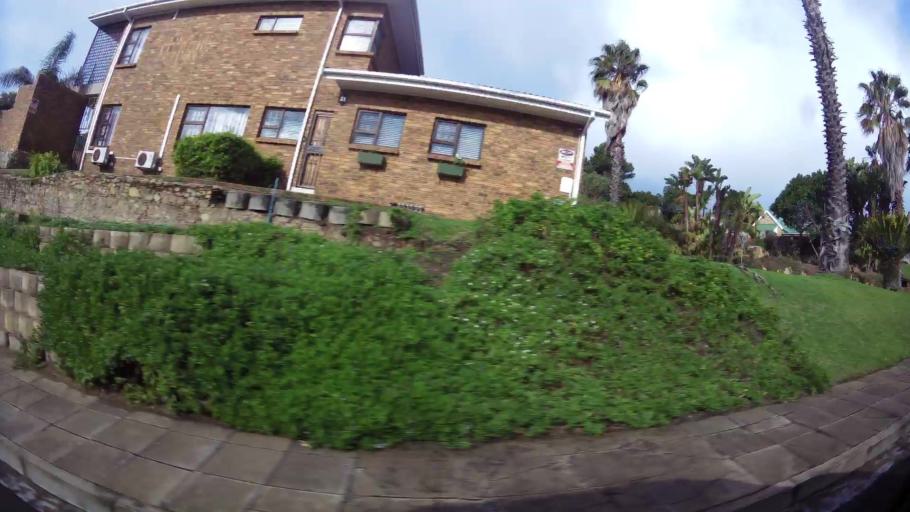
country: ZA
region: Western Cape
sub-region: Eden District Municipality
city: Mossel Bay
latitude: -34.1862
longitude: 22.1400
